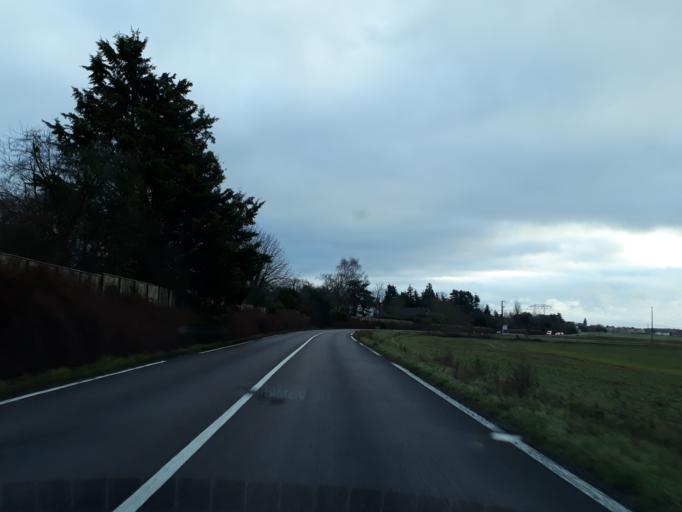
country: FR
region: Ile-de-France
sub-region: Departement de l'Essonne
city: Gometz-la-Ville
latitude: 48.6757
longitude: 2.1027
